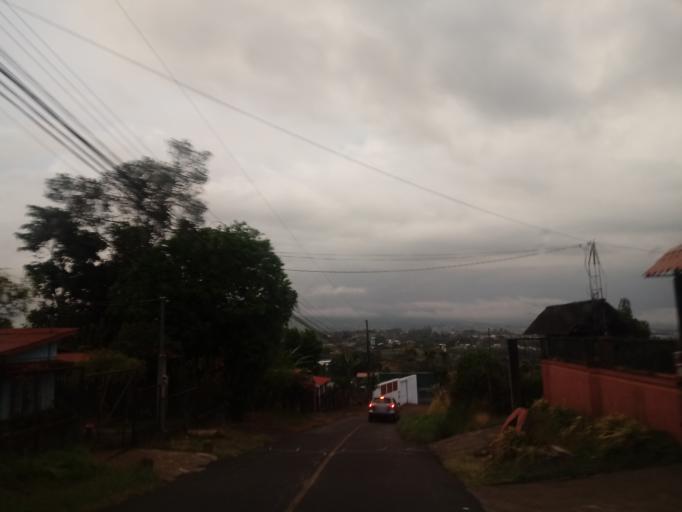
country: CR
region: Heredia
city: Angeles
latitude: 10.0243
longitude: -84.0402
